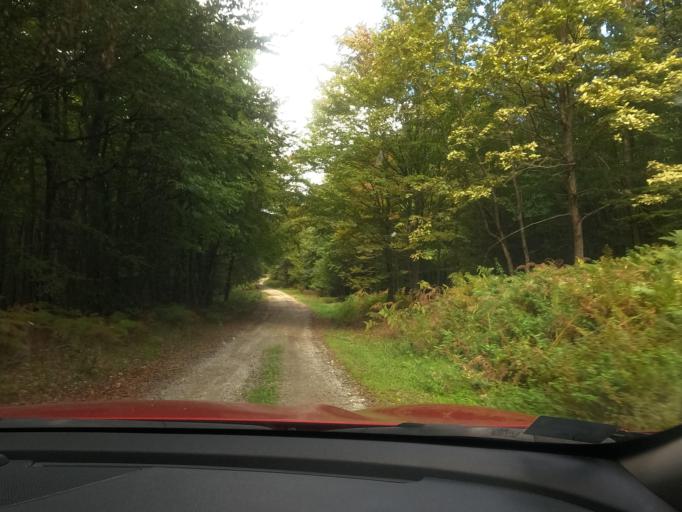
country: BA
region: Federation of Bosnia and Herzegovina
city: Velika Kladusa
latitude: 45.2621
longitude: 15.7843
